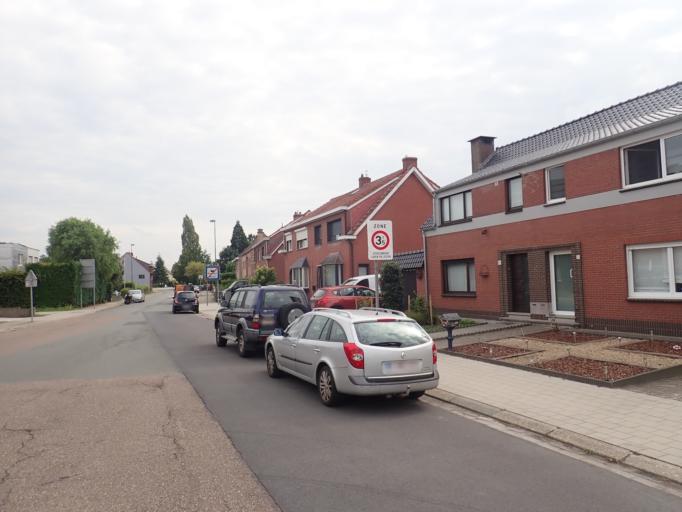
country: BE
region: Flanders
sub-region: Provincie Antwerpen
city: Wommelgem
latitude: 51.2103
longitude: 4.5139
